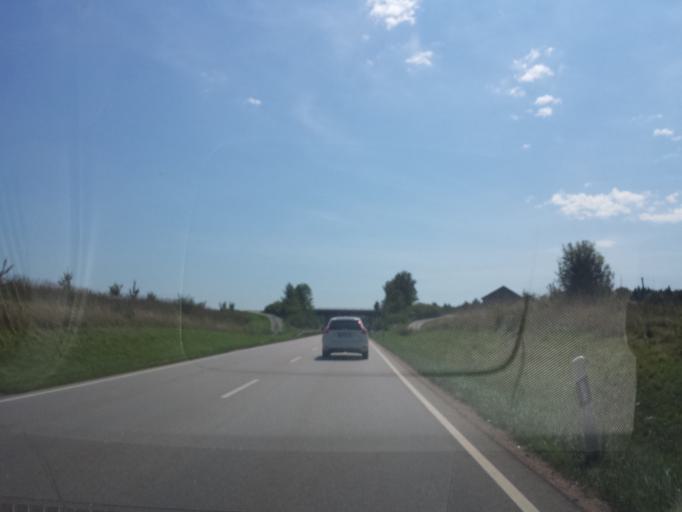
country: DE
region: Bavaria
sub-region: Lower Bavaria
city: Ascha
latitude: 48.9936
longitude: 12.6298
